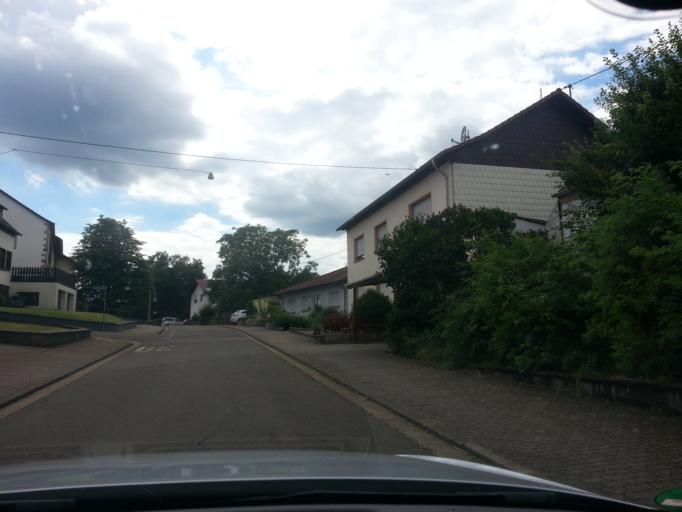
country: DE
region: Saarland
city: Nalbach
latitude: 49.4115
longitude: 6.7664
